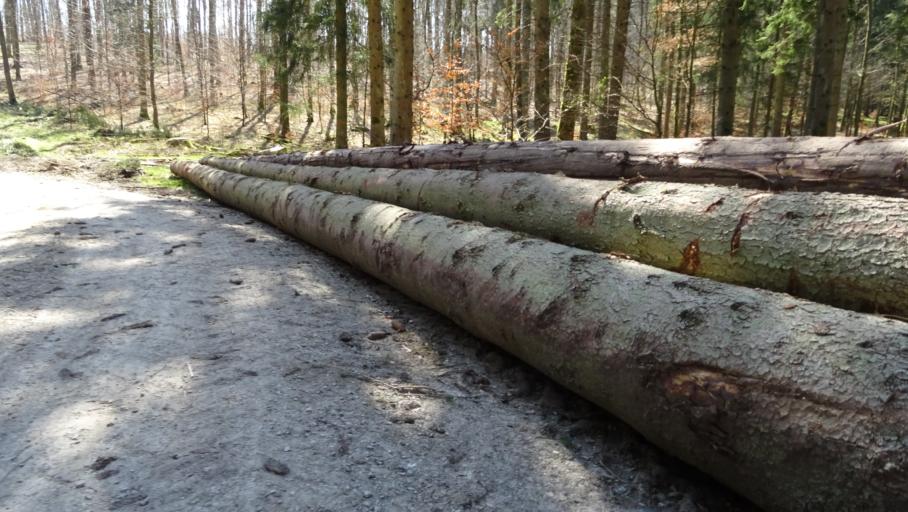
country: DE
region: Baden-Wuerttemberg
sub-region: Regierungsbezirk Stuttgart
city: Roigheim
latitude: 49.4007
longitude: 9.3355
